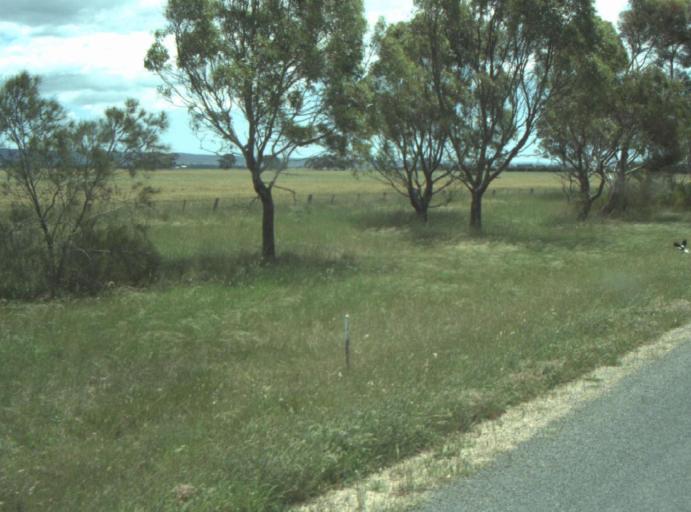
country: AU
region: Victoria
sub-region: Greater Geelong
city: Lara
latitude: -37.8780
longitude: 144.3802
